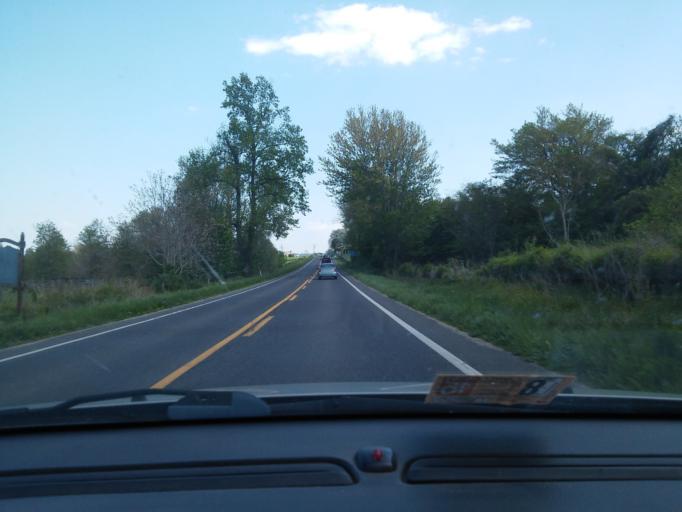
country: US
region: Virginia
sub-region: Rappahannock County
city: Washington
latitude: 38.6545
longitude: -78.2220
